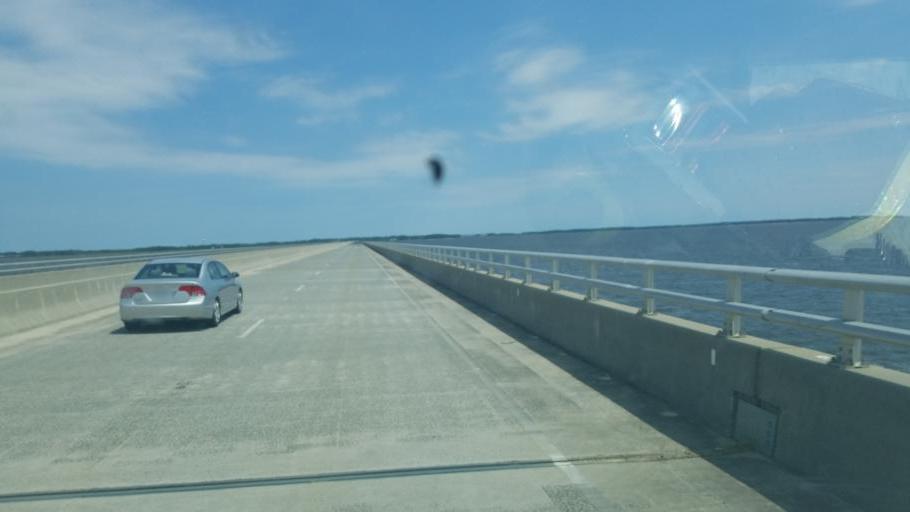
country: US
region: North Carolina
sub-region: Dare County
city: Manteo
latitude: 35.8840
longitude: -75.7043
